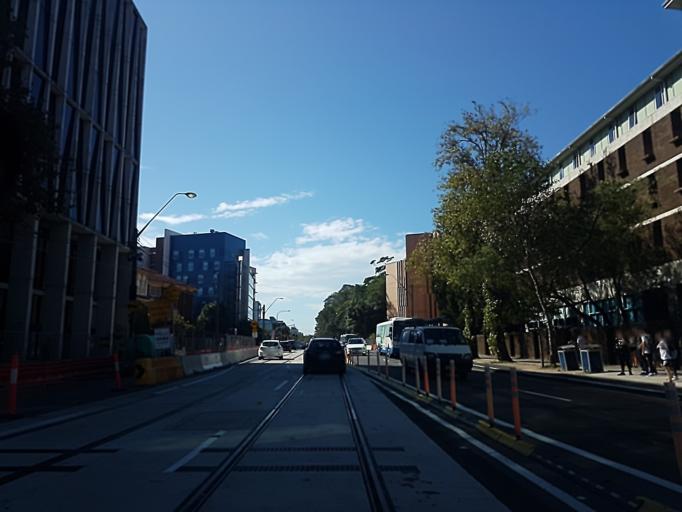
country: AU
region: New South Wales
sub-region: Randwick
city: Kensington
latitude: -33.9187
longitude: 151.2263
